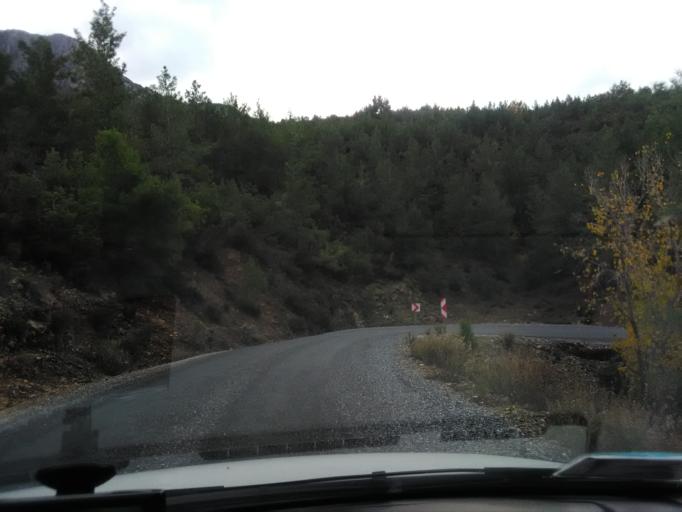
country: TR
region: Antalya
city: Gazipasa
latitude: 36.3053
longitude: 32.3991
